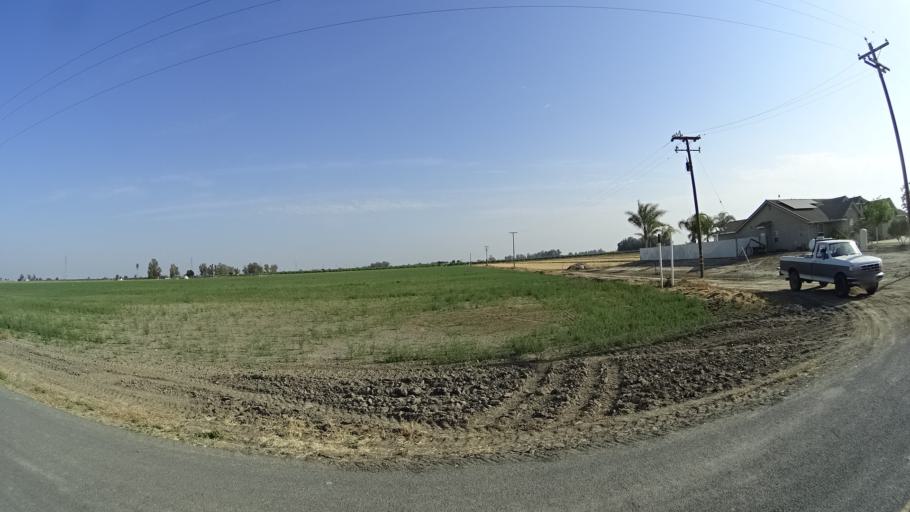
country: US
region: California
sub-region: Fresno County
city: Riverdale
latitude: 36.3584
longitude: -119.8830
